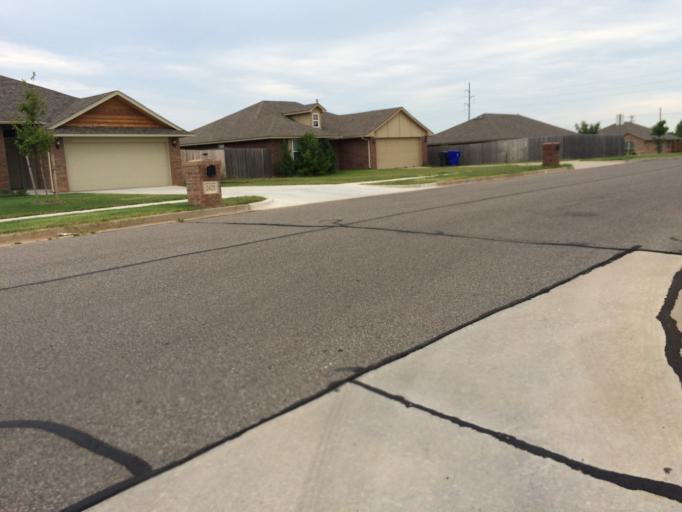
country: US
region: Oklahoma
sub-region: Cleveland County
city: Hall Park
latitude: 35.2486
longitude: -97.4189
